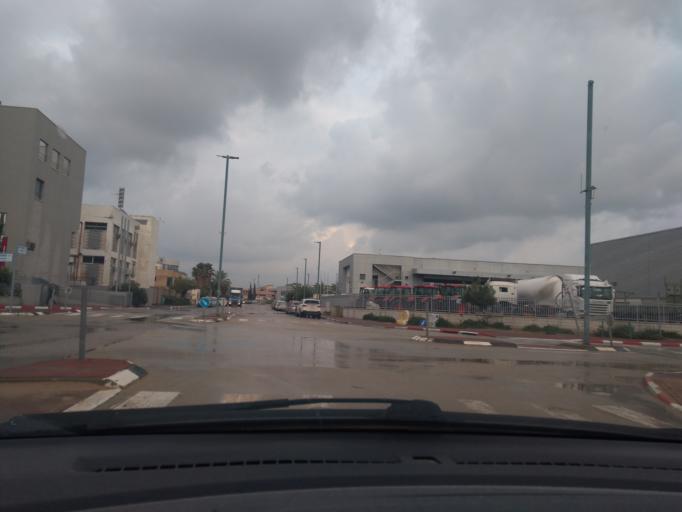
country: IL
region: Central District
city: Elyakhin
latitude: 32.4008
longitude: 34.8949
